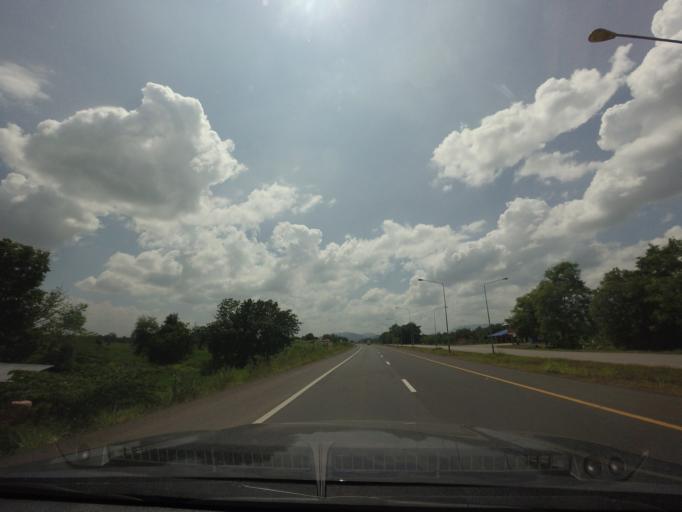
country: TH
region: Phetchabun
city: Phetchabun
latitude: 16.4455
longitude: 101.1102
